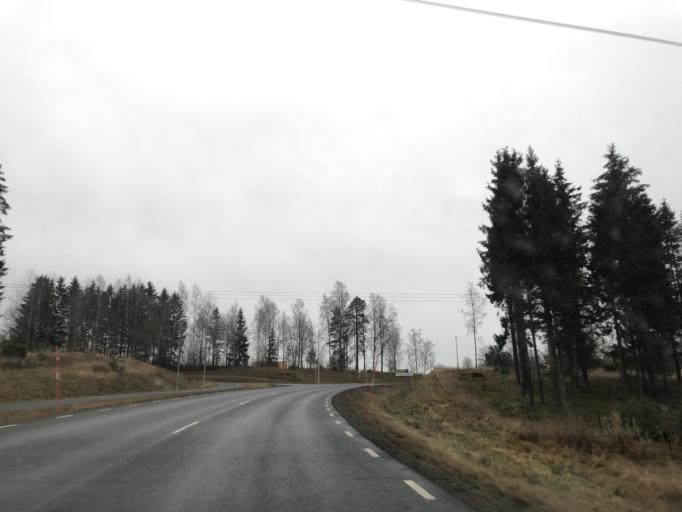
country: SE
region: Vaestra Goetaland
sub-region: Ulricehamns Kommun
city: Ulricehamn
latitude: 57.8154
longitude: 13.2892
